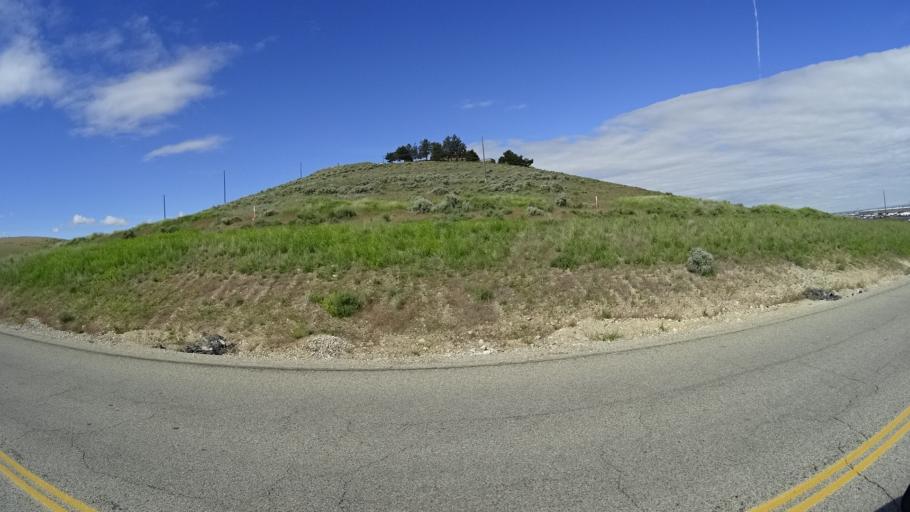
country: US
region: Idaho
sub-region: Ada County
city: Boise
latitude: 43.5105
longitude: -116.1480
